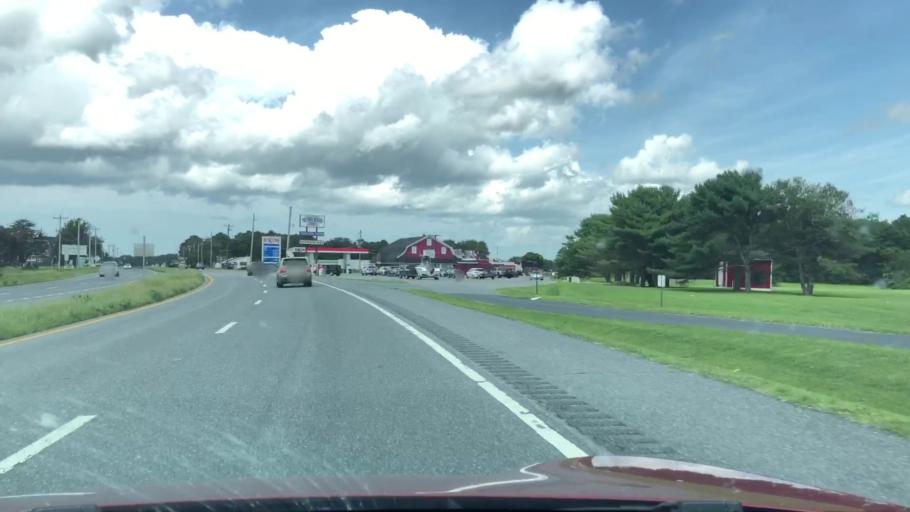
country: US
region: Virginia
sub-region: Northampton County
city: Cape Charles
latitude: 37.2117
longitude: -75.9662
